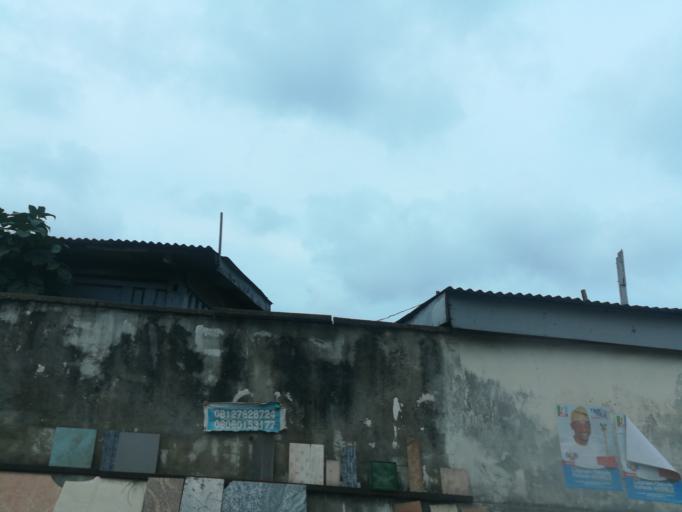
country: NG
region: Lagos
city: Ojota
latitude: 6.5642
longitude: 3.3654
